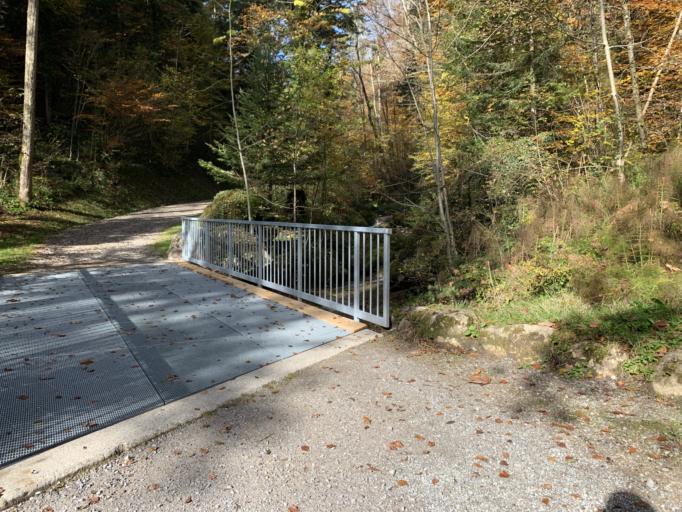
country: CH
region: Zurich
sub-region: Bezirk Hinwil
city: Hinwil
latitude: 47.3070
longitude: 8.8547
